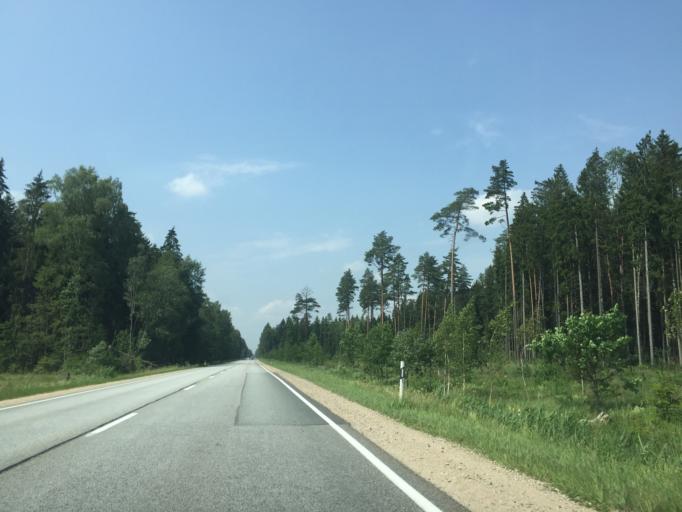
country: LV
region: Kekava
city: Kekava
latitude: 56.8121
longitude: 24.1582
